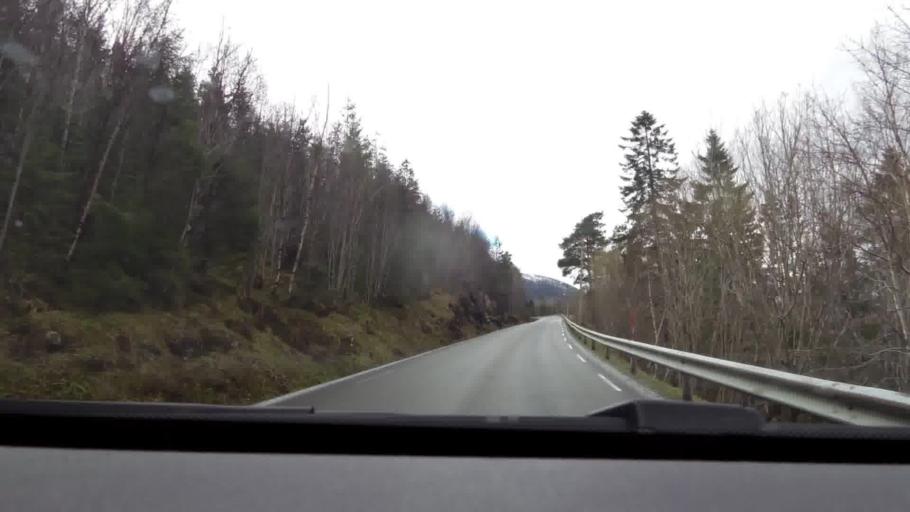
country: NO
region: More og Romsdal
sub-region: Eide
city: Eide
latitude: 62.9193
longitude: 7.5537
